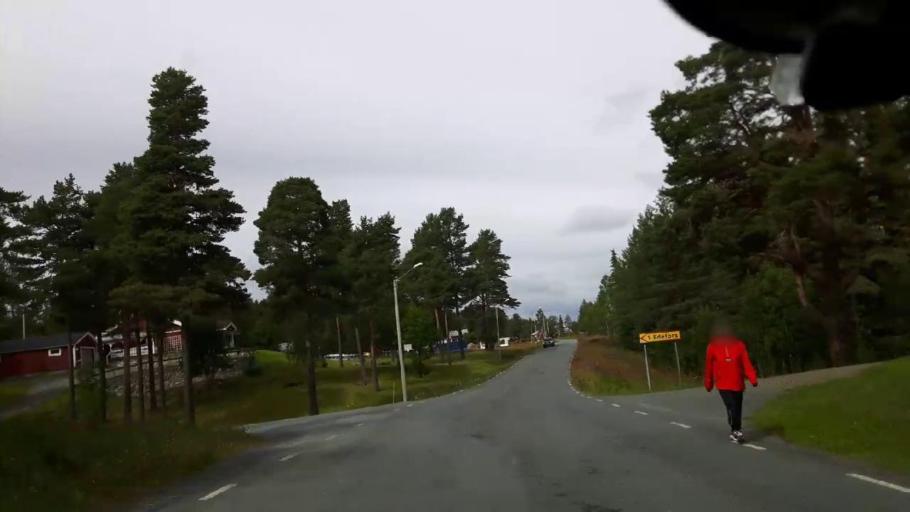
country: SE
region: Jaemtland
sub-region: Krokoms Kommun
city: Valla
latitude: 63.4607
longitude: 14.0330
